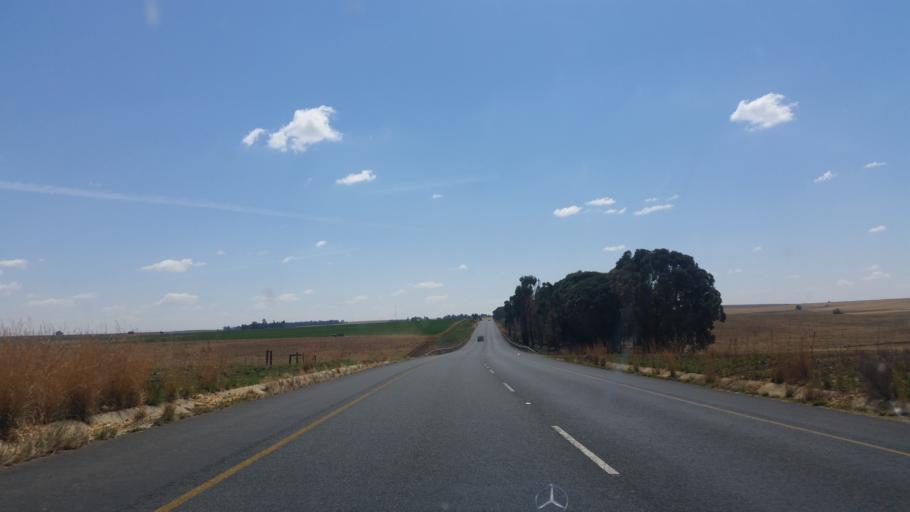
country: ZA
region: Orange Free State
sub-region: Thabo Mofutsanyana District Municipality
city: Bethlehem
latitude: -28.1011
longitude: 28.6584
